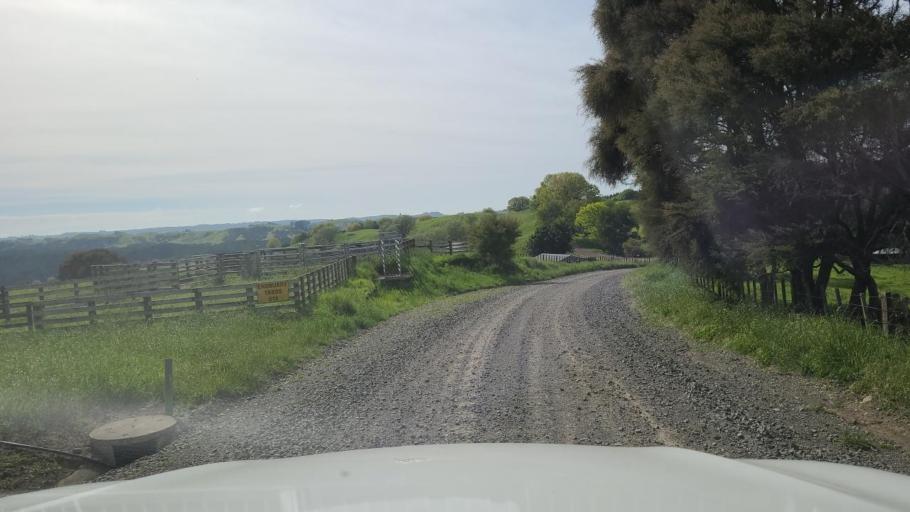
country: NZ
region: Hawke's Bay
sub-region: Napier City
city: Taradale
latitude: -39.3495
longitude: 176.6768
